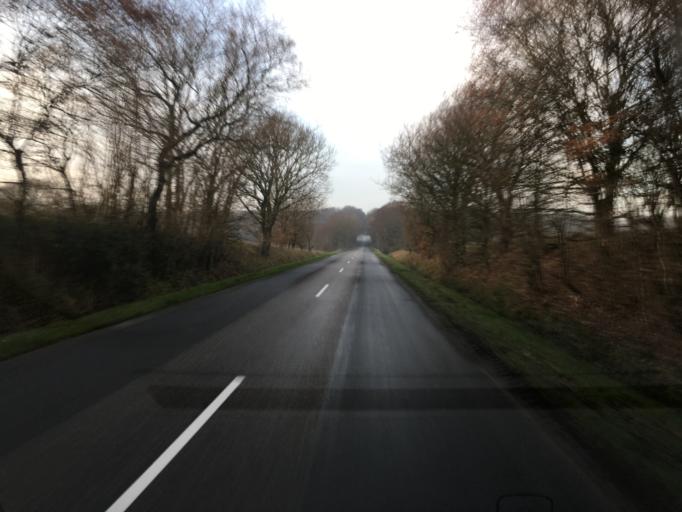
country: DK
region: South Denmark
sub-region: Tonder Kommune
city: Toftlund
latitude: 55.1400
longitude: 9.0557
